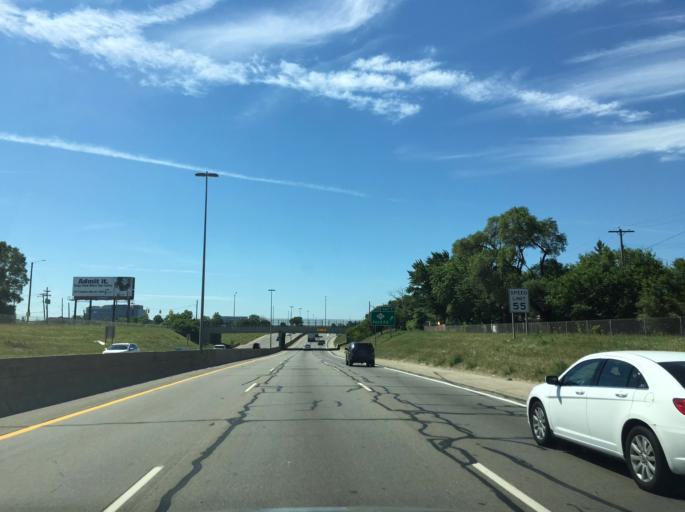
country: US
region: Michigan
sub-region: Wayne County
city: Dearborn
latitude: 42.3377
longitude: -83.2161
